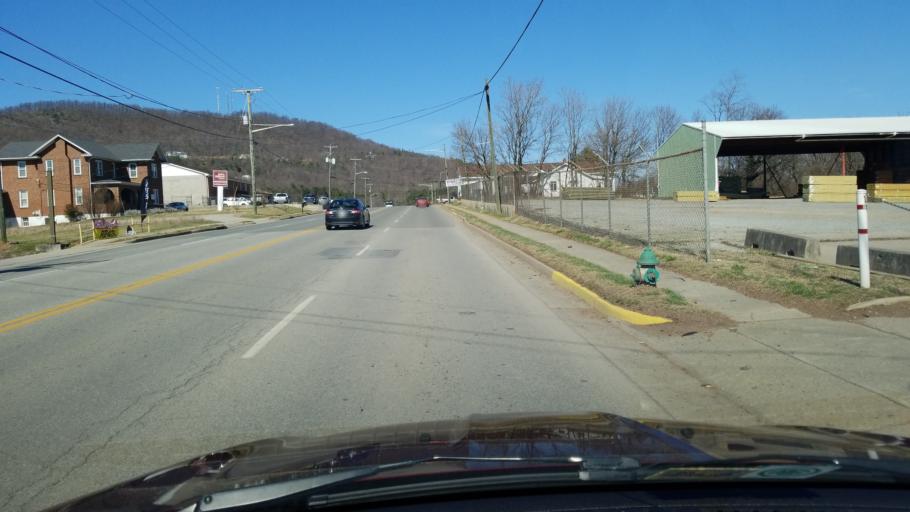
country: US
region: Virginia
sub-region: Franklin County
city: Rocky Mount
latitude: 37.0108
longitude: -79.8934
